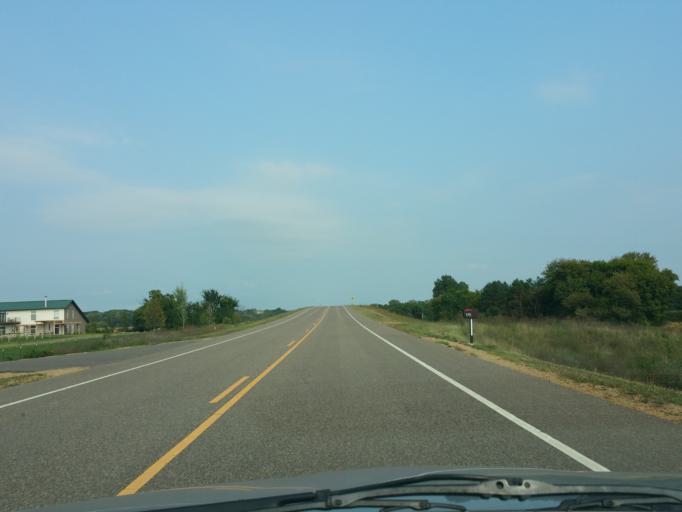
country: US
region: Minnesota
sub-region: Washington County
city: Lake Saint Croix Beach
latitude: 44.9310
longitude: -92.6898
